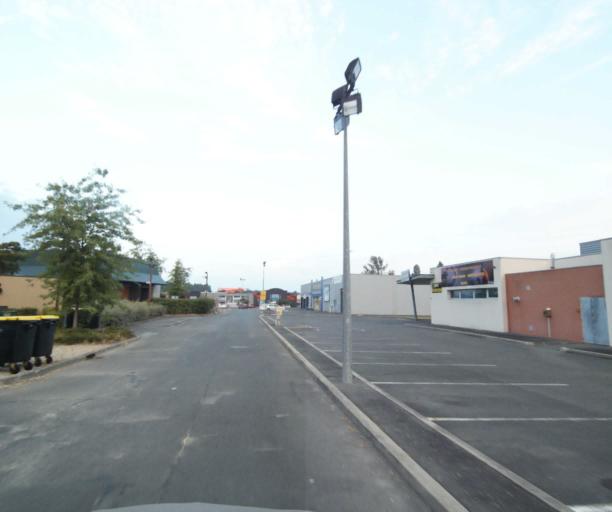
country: FR
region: Aquitaine
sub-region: Departement de la Gironde
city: Creon
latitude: 44.7723
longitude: -0.3343
